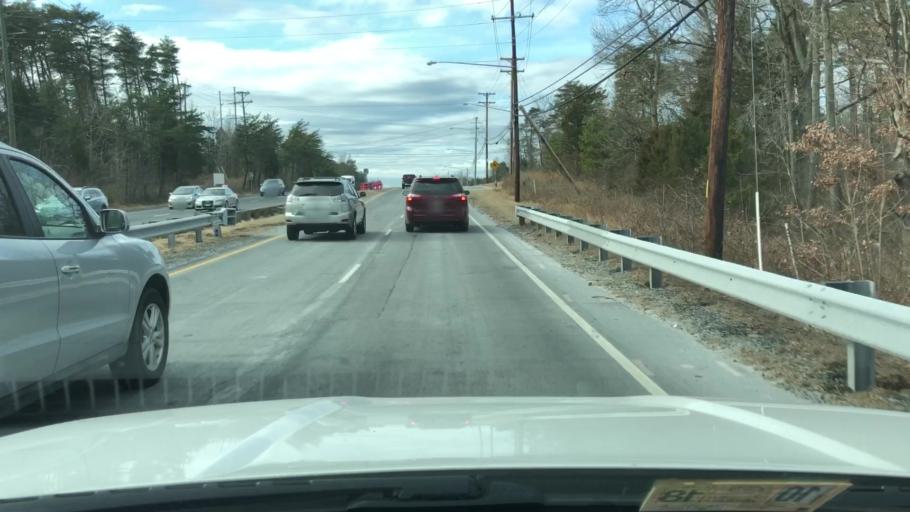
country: US
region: Virginia
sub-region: Fairfax County
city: Centreville
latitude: 38.8332
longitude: -77.4639
